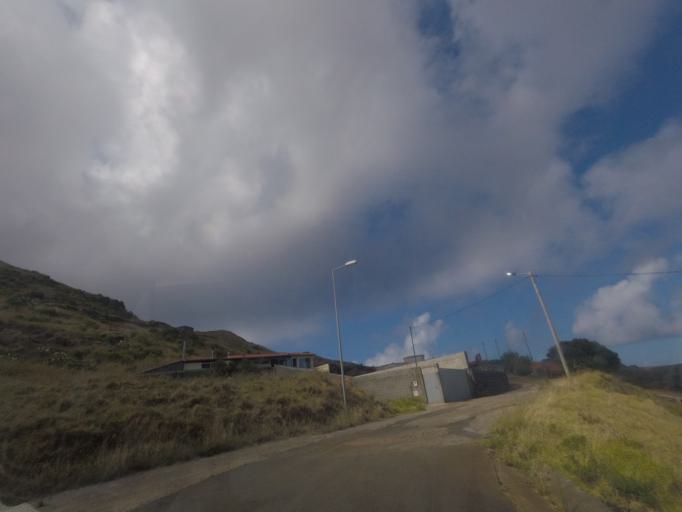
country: PT
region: Madeira
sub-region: Machico
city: Canical
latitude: 32.7431
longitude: -16.7468
